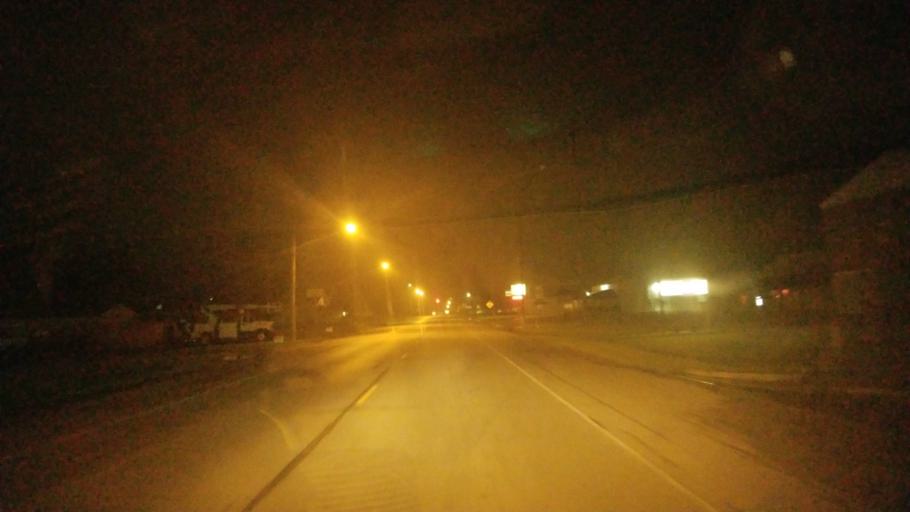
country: US
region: Missouri
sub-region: Pike County
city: Bowling Green
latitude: 39.3472
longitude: -91.2055
